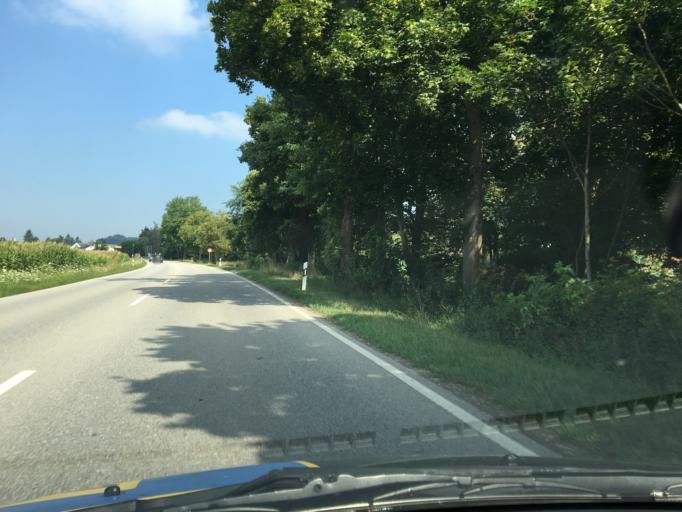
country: DE
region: Bavaria
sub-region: Upper Bavaria
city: Winhoring
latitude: 48.2609
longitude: 12.6604
